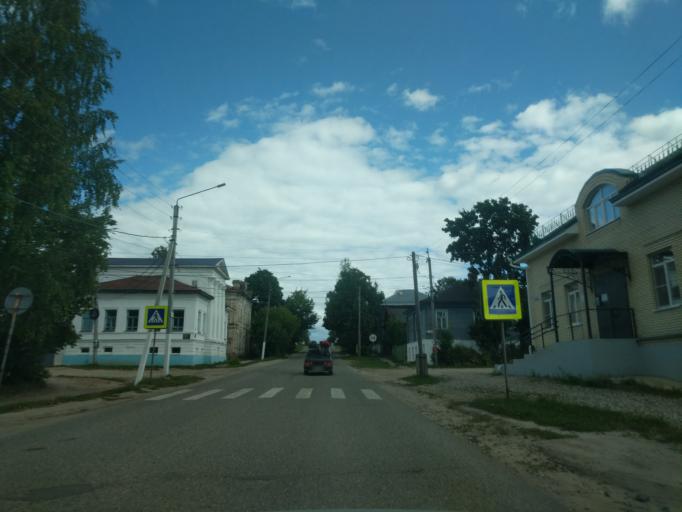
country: RU
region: Kostroma
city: Sudislavl'
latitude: 57.8816
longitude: 41.7121
